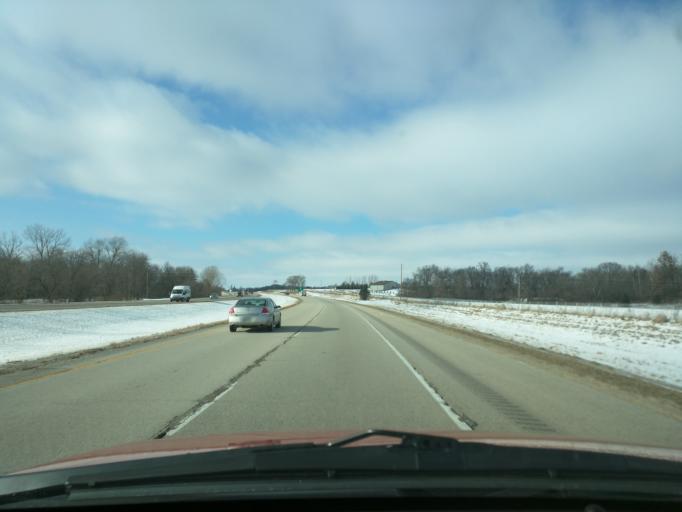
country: US
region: Minnesota
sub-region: Goodhue County
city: Pine Island
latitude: 44.1999
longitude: -92.6125
